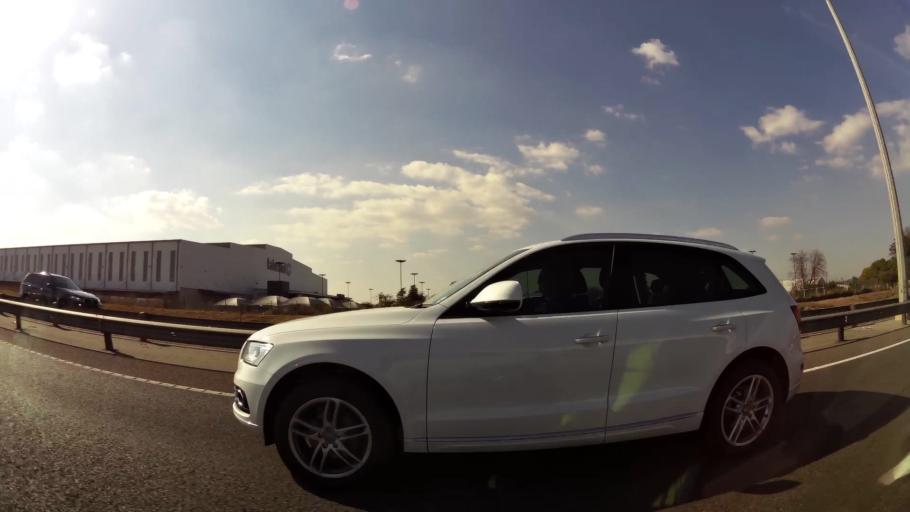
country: ZA
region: Gauteng
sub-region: Ekurhuleni Metropolitan Municipality
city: Tembisa
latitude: -26.0776
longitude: 28.2722
